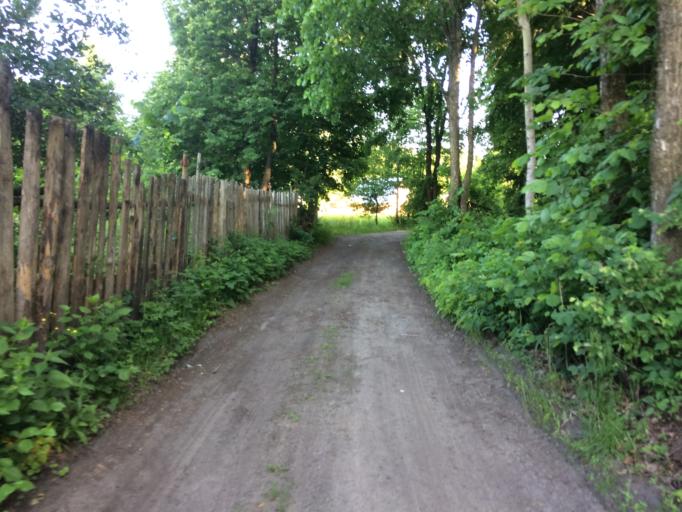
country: RU
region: Mariy-El
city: Mochalishche
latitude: 56.5444
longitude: 48.4117
